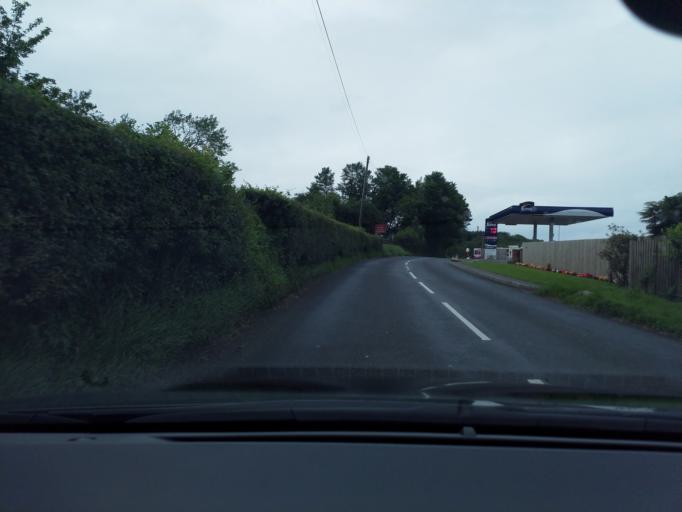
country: GB
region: Northern Ireland
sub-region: Dungannon District
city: Dungannon
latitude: 54.4449
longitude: -6.7952
